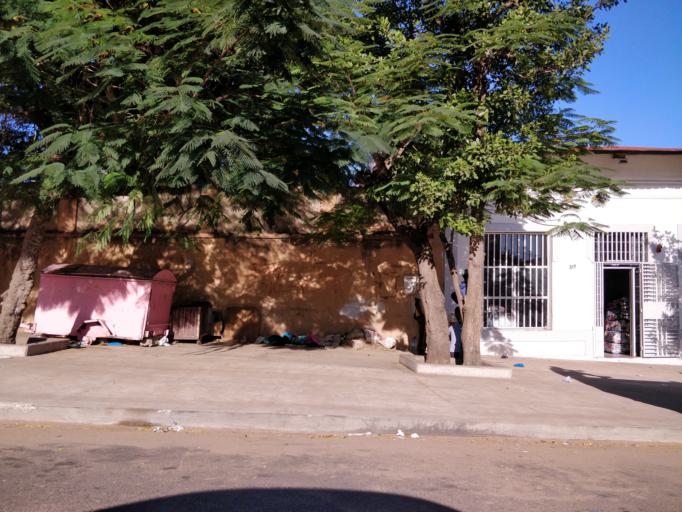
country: MZ
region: Maputo City
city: Maputo
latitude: -25.9664
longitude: 32.5666
